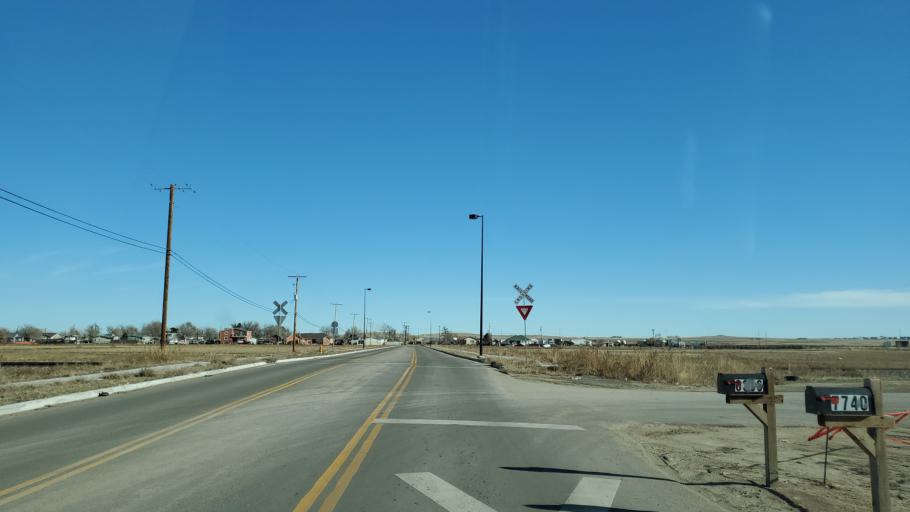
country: US
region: Colorado
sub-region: Adams County
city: Derby
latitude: 39.8490
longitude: -104.8977
